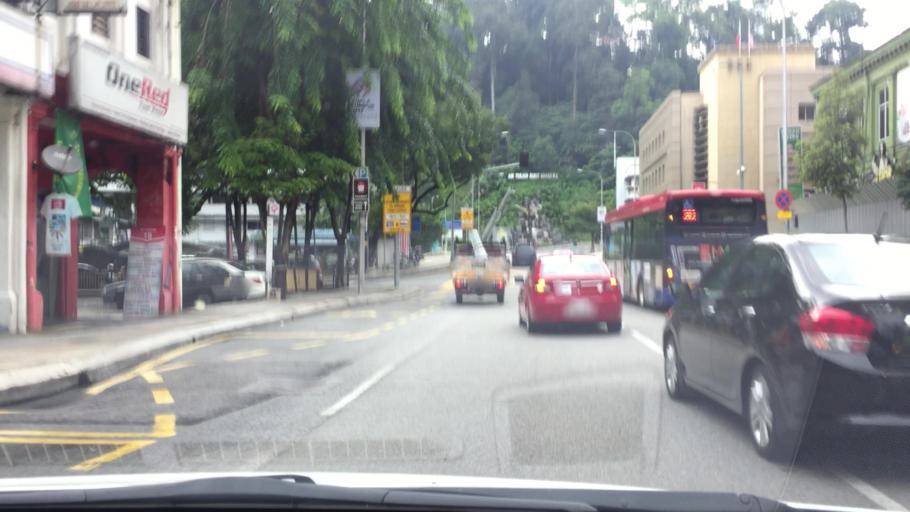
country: MY
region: Kuala Lumpur
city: Kuala Lumpur
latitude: 3.1560
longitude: 101.7003
